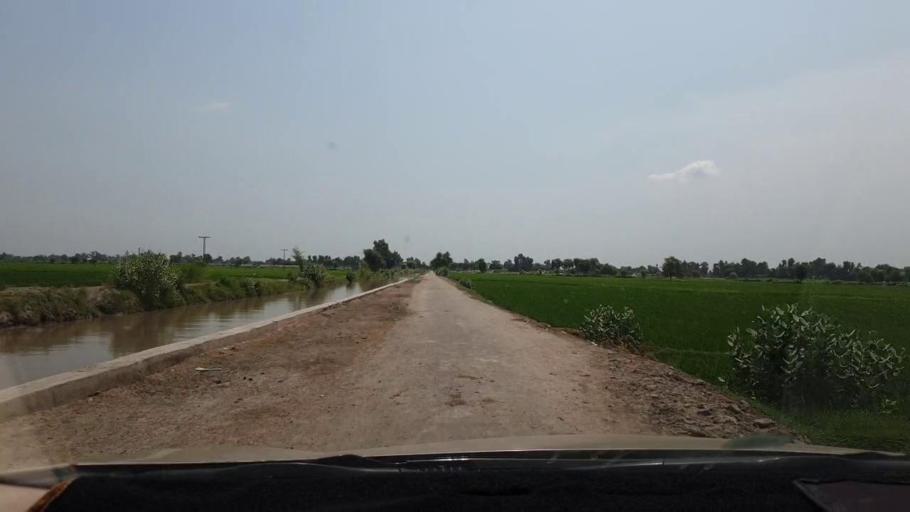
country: PK
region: Sindh
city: Naudero
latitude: 27.6598
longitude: 68.3258
